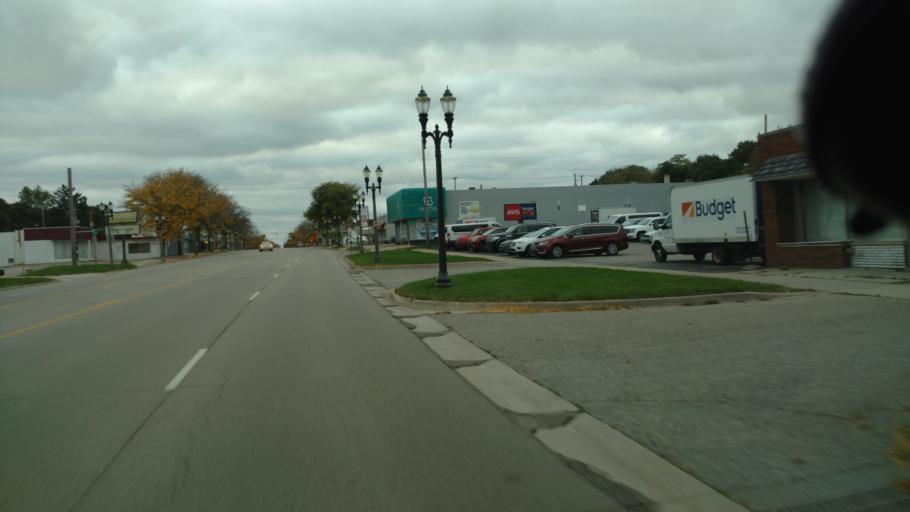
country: US
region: Michigan
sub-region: Ingham County
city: East Lansing
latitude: 42.7336
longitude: -84.5142
